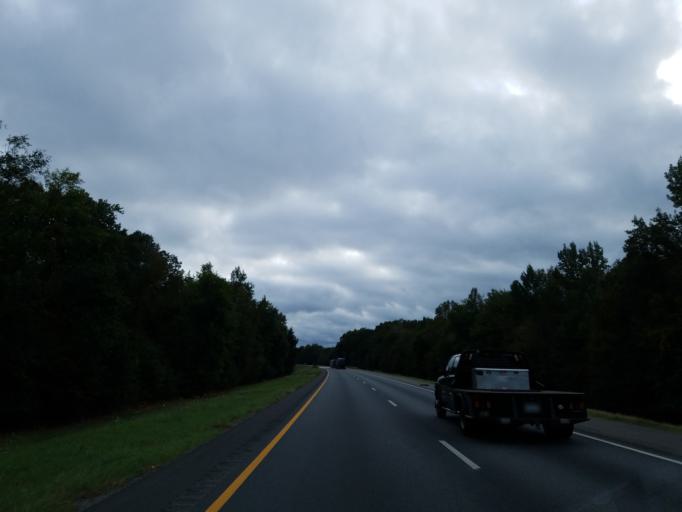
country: US
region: Alabama
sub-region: Tuscaloosa County
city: Tuscaloosa
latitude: 33.1281
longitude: -87.6454
